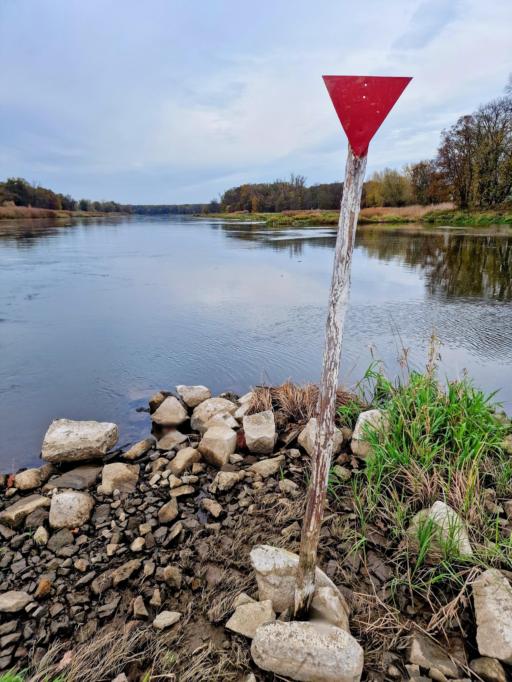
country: PL
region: Lubusz
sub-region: Powiat zielonogorski
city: Klenica
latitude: 51.9648
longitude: 15.7703
